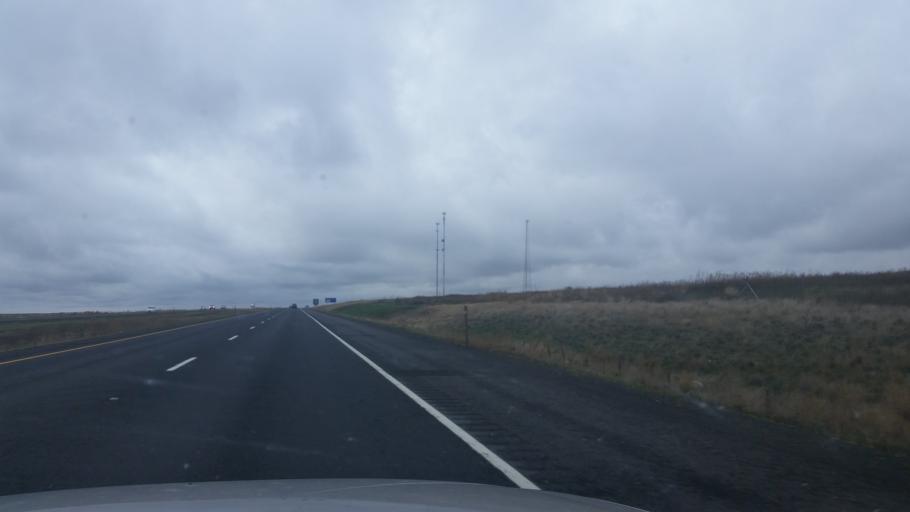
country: US
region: Washington
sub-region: Spokane County
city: Medical Lake
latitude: 47.3216
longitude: -117.9442
